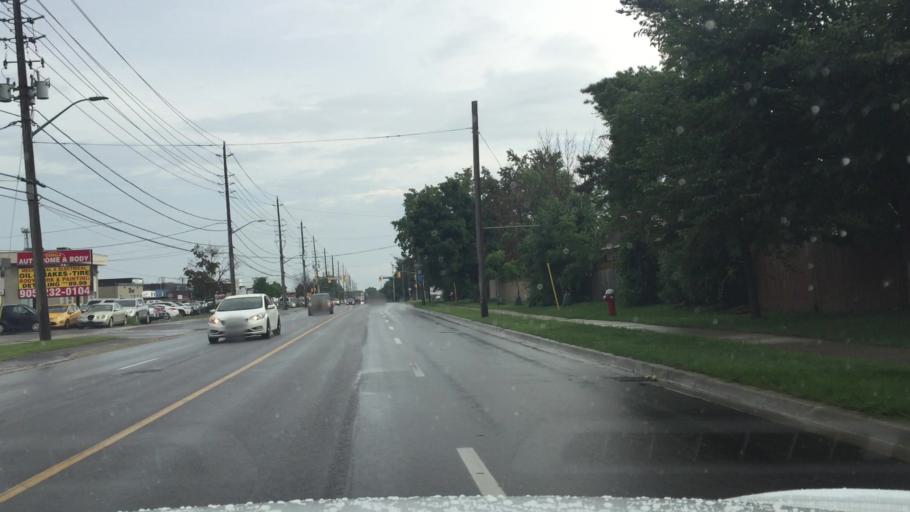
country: CA
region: Ontario
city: Mississauga
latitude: 43.5681
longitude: -79.6433
